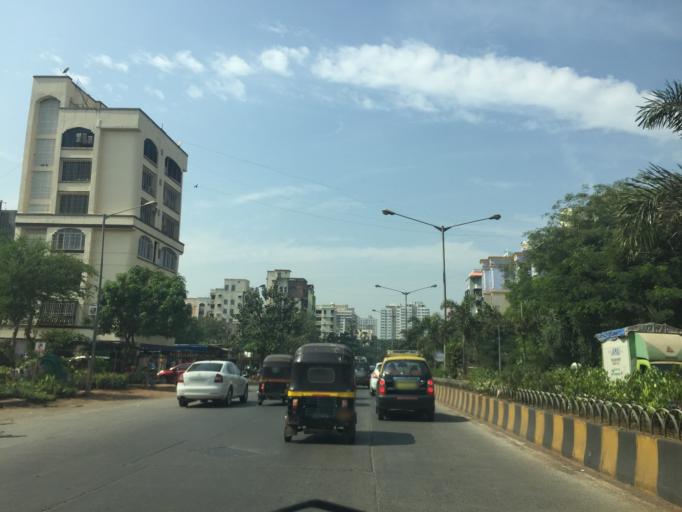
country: IN
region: Maharashtra
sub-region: Mumbai Suburban
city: Borivli
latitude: 19.2198
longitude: 72.8438
